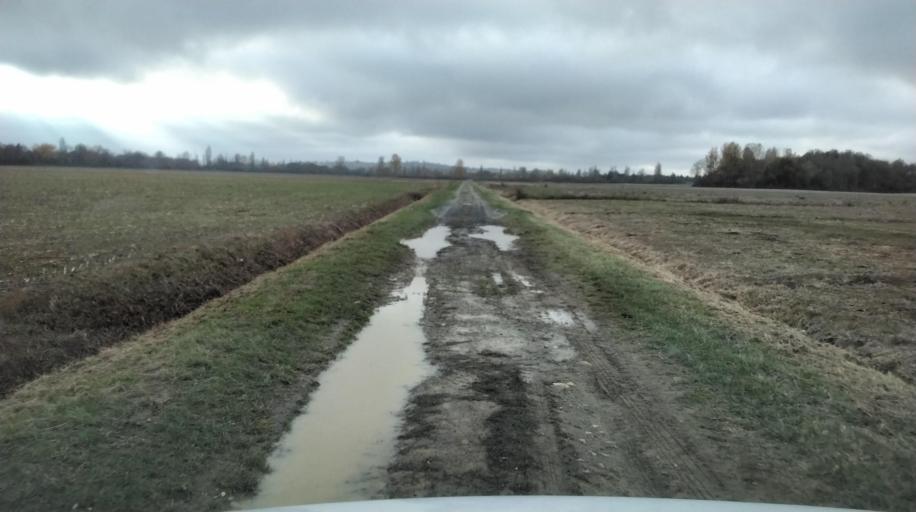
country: FR
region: Midi-Pyrenees
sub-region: Departement de la Haute-Garonne
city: Le Fousseret
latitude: 43.2680
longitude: 1.0391
